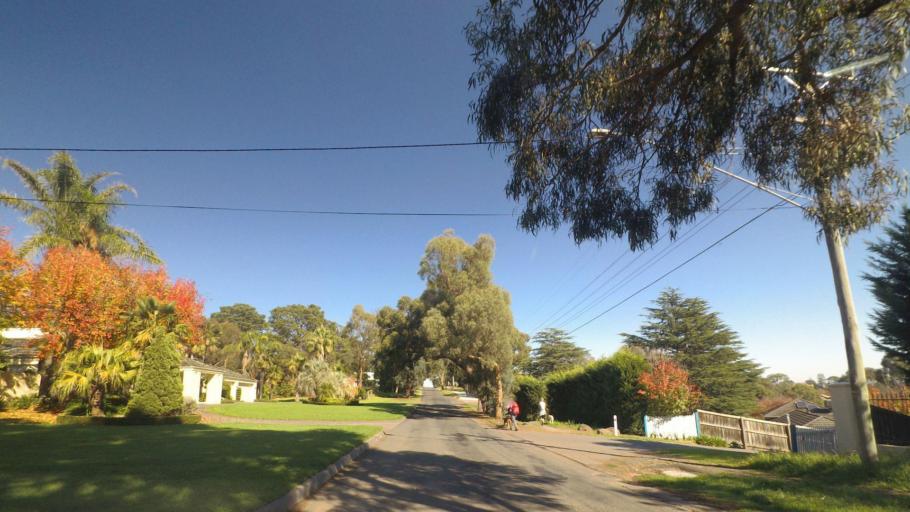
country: AU
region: Victoria
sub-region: Nillumbik
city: Eltham
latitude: -37.7503
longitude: 145.1553
